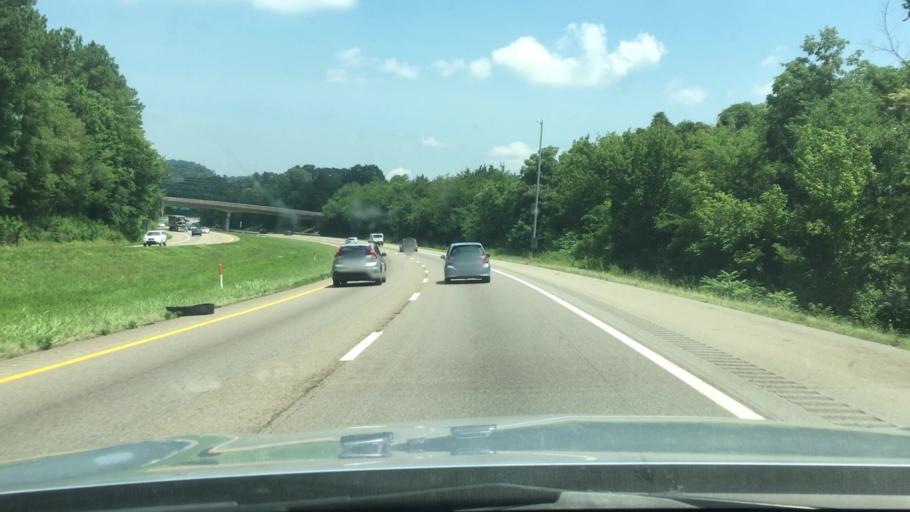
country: US
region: Tennessee
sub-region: Loudon County
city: Lenoir City
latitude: 35.8597
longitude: -84.2592
